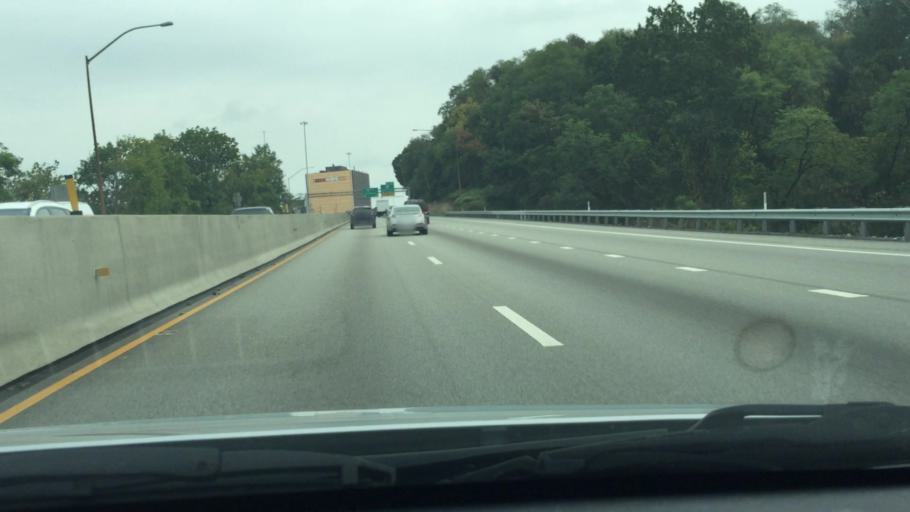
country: US
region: Pennsylvania
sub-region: Allegheny County
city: Green Tree
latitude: 40.4181
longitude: -80.0548
